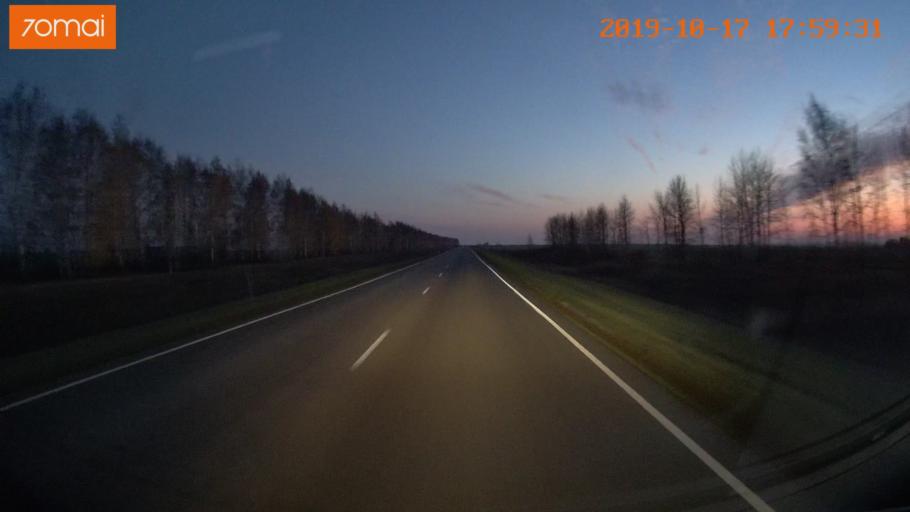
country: RU
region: Tula
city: Kurkino
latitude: 53.5372
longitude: 38.6212
